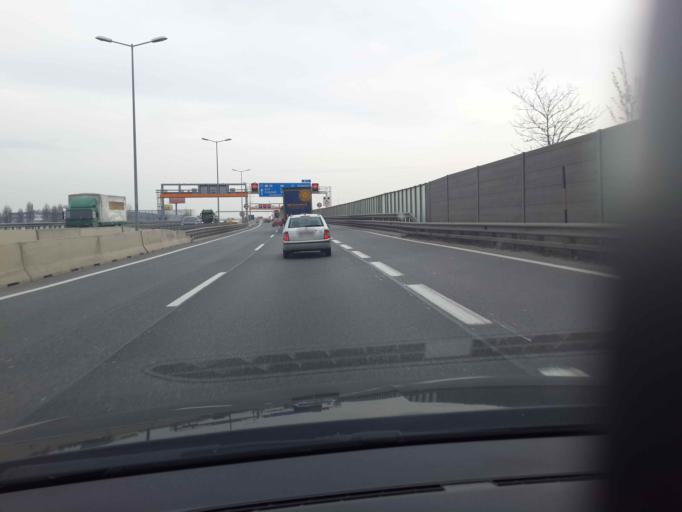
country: AT
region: Lower Austria
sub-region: Politischer Bezirk Wien-Umgebung
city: Schwechat
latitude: 48.1440
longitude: 16.4867
